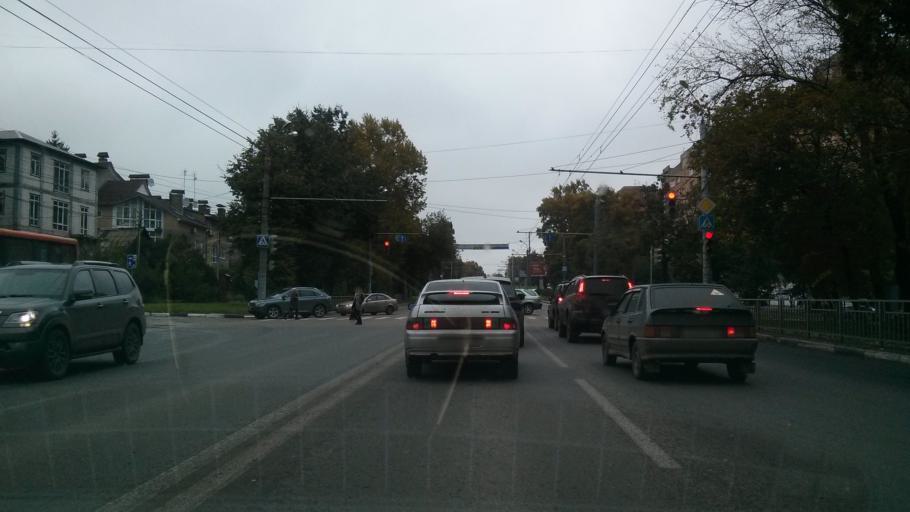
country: RU
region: Nizjnij Novgorod
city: Nizhniy Novgorod
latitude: 56.3211
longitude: 44.0465
